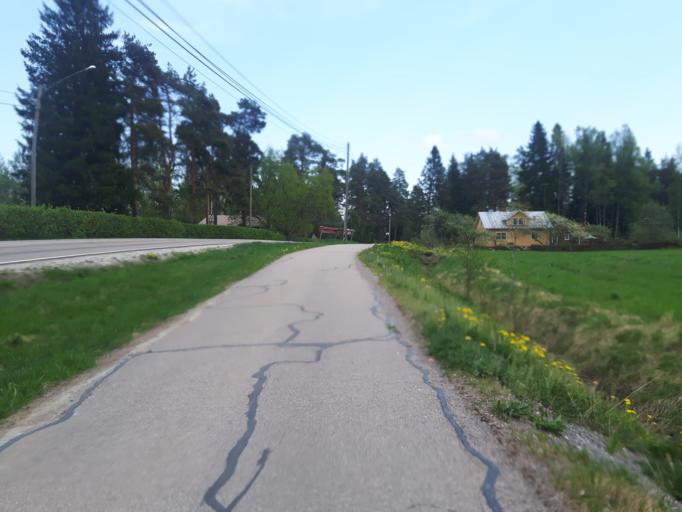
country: FI
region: Uusimaa
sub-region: Porvoo
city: Porvoo
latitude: 60.3938
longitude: 25.7405
